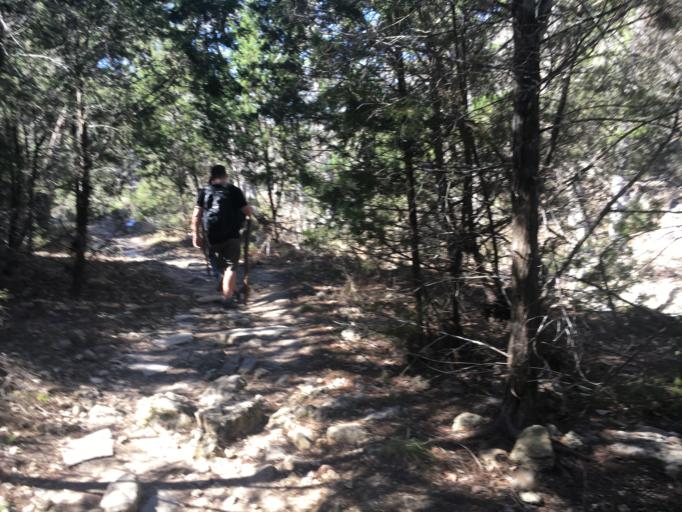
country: US
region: Texas
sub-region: Travis County
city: Briarcliff
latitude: 30.3432
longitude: -98.1289
